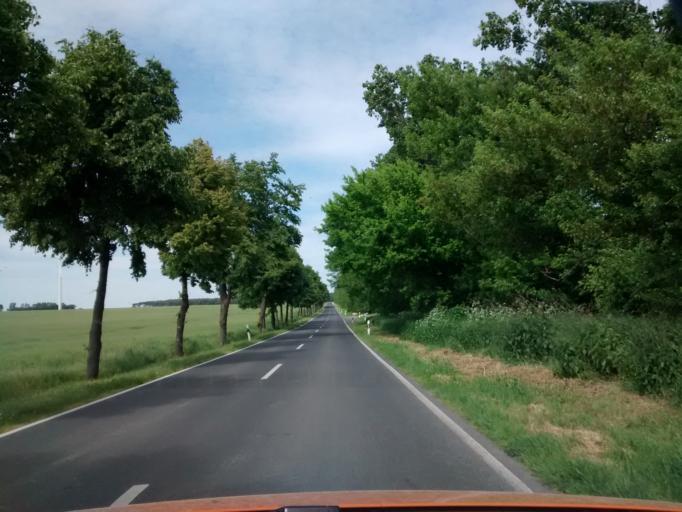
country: DE
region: Brandenburg
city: Ihlow
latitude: 51.8953
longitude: 13.3085
